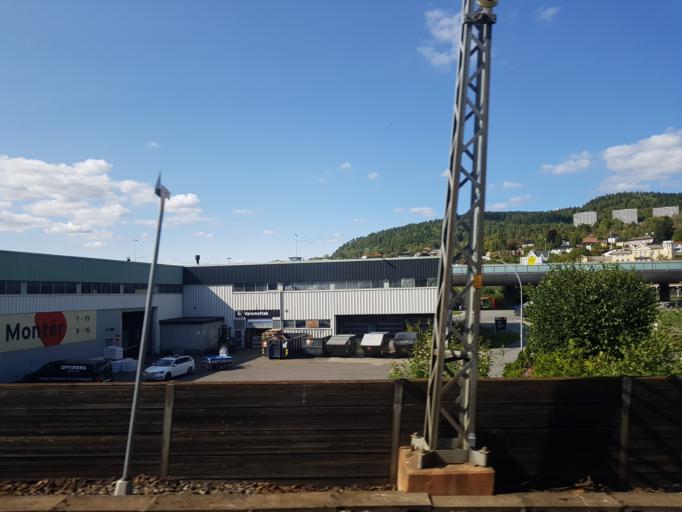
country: NO
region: Buskerud
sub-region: Drammen
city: Drammen
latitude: 59.7415
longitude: 10.2306
